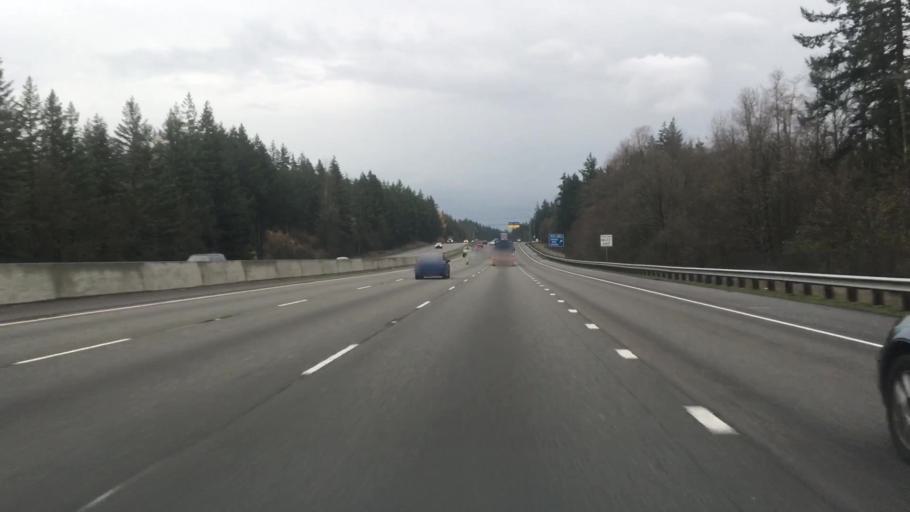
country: US
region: Washington
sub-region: Thurston County
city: Grand Mound
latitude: 46.8776
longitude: -122.9671
